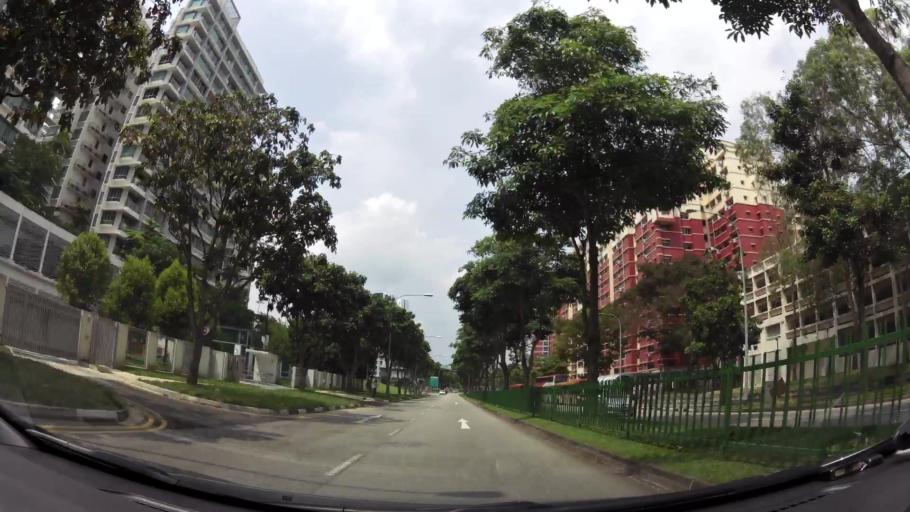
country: MY
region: Johor
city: Kampung Pasir Gudang Baru
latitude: 1.3733
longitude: 103.9440
